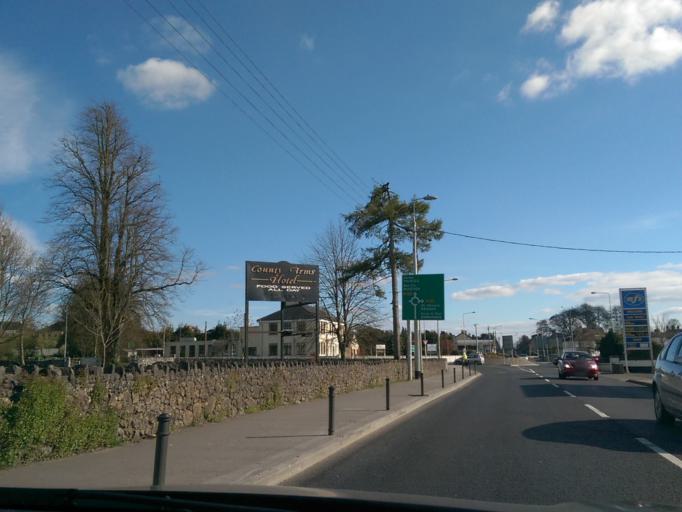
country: IE
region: Leinster
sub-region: Uibh Fhaili
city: Birr
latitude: 53.0904
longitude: -7.9075
